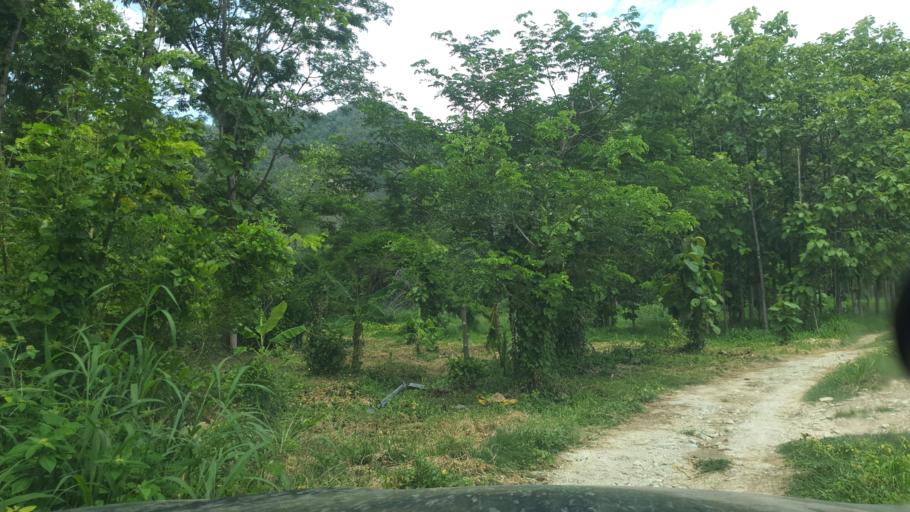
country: TH
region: Lampang
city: Sop Prap
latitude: 17.8554
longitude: 99.3969
